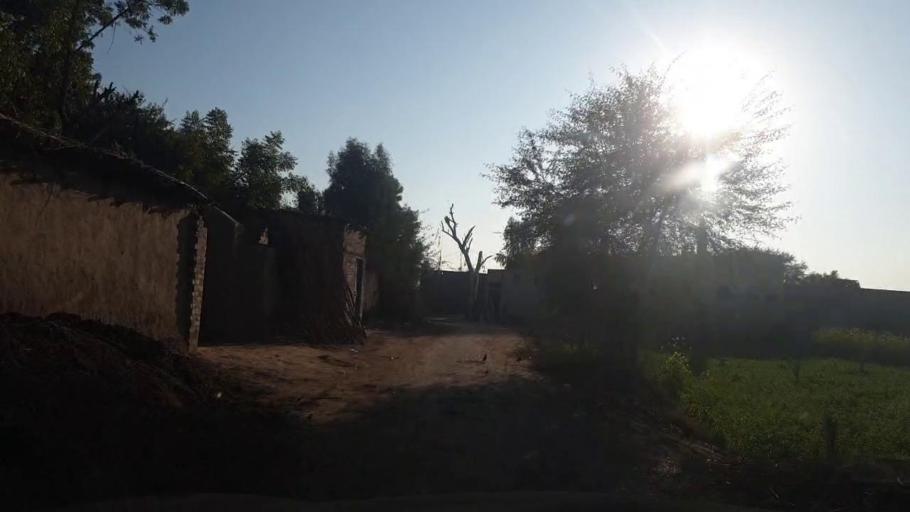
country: PK
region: Sindh
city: Ghotki
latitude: 28.0972
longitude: 69.3610
